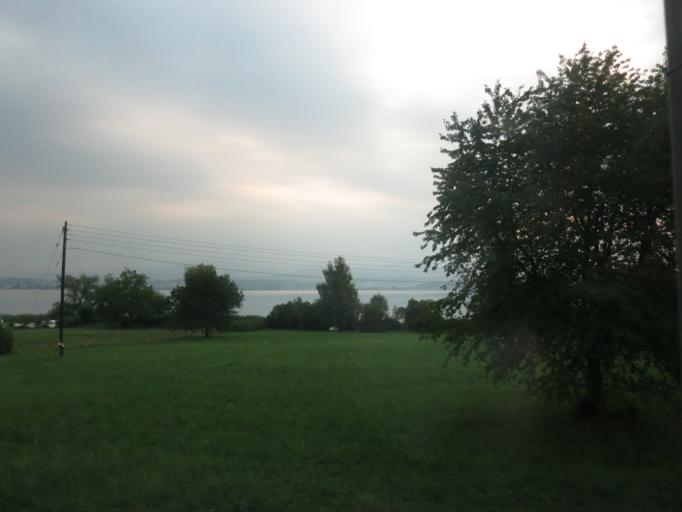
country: CH
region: Schwyz
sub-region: Bezirk March
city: Altendorf
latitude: 47.1931
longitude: 8.8335
